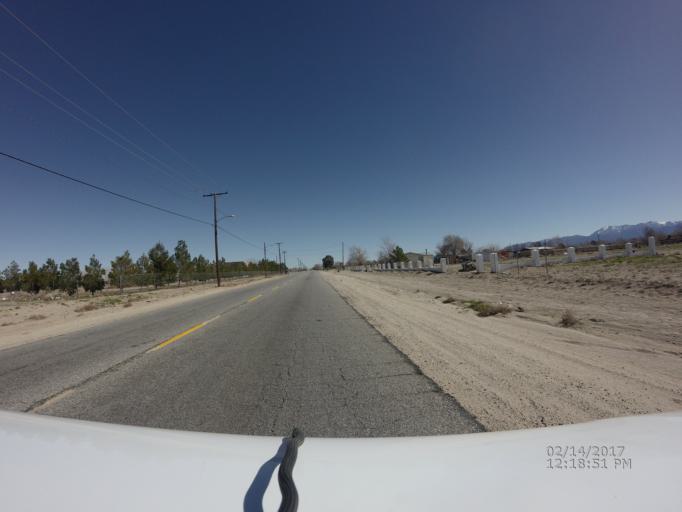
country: US
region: California
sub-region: Los Angeles County
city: Littlerock
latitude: 34.5798
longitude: -117.9542
